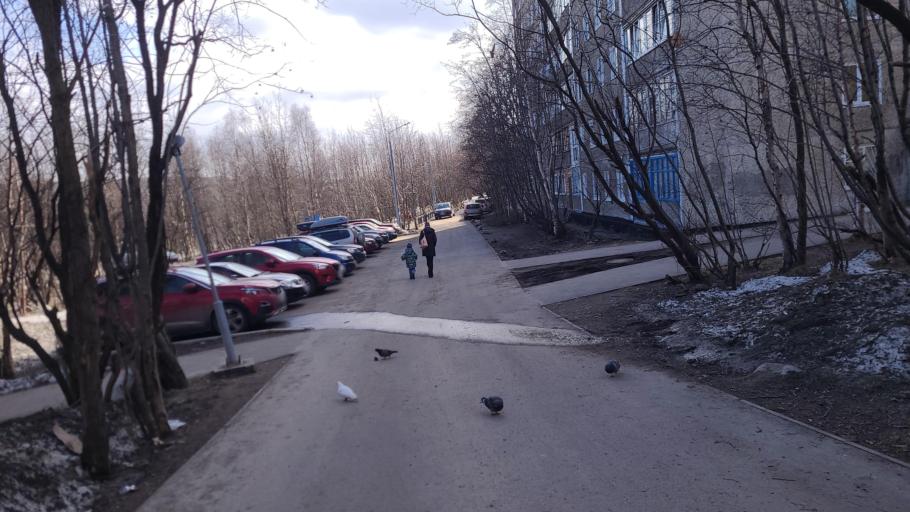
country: RU
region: Murmansk
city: Murmansk
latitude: 68.9418
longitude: 33.1011
